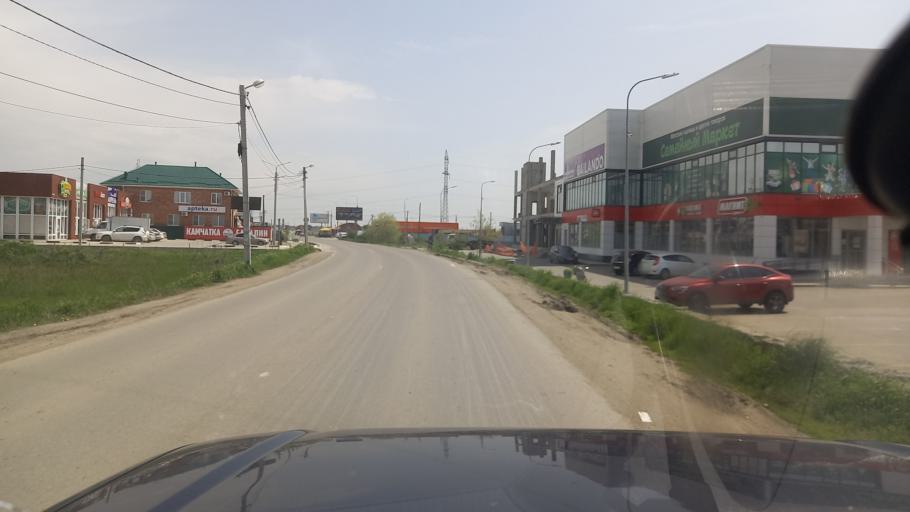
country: RU
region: Adygeya
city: Yablonovskiy
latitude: 44.9861
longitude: 38.9632
